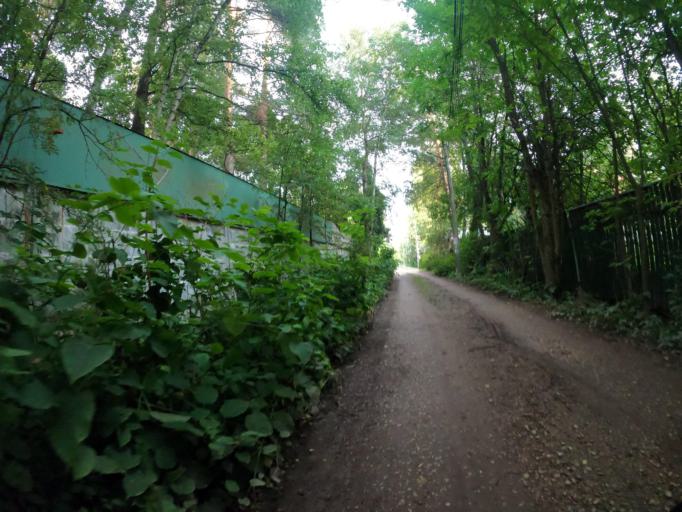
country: RU
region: Moskovskaya
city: Il'inskiy
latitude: 55.6436
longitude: 38.1103
